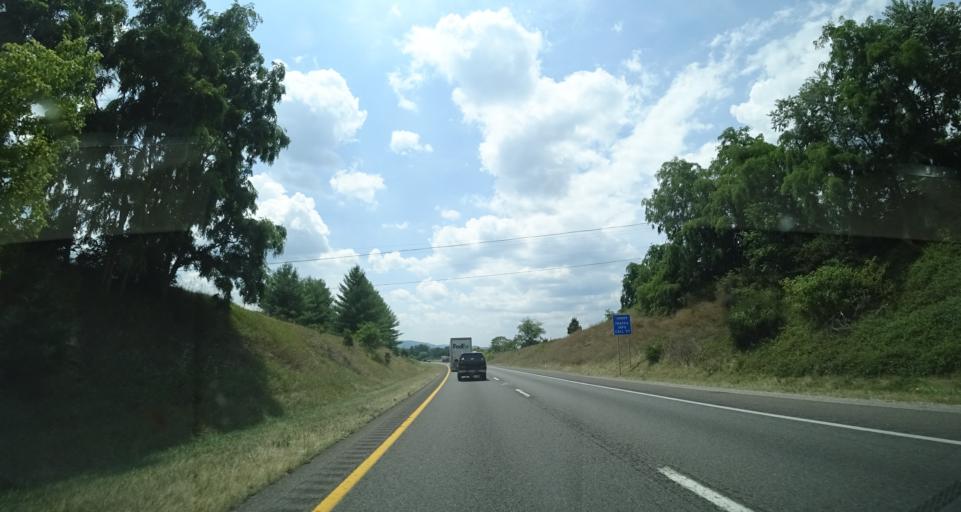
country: US
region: Virginia
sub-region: Pulaski County
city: Dublin
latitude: 37.0749
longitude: -80.7009
